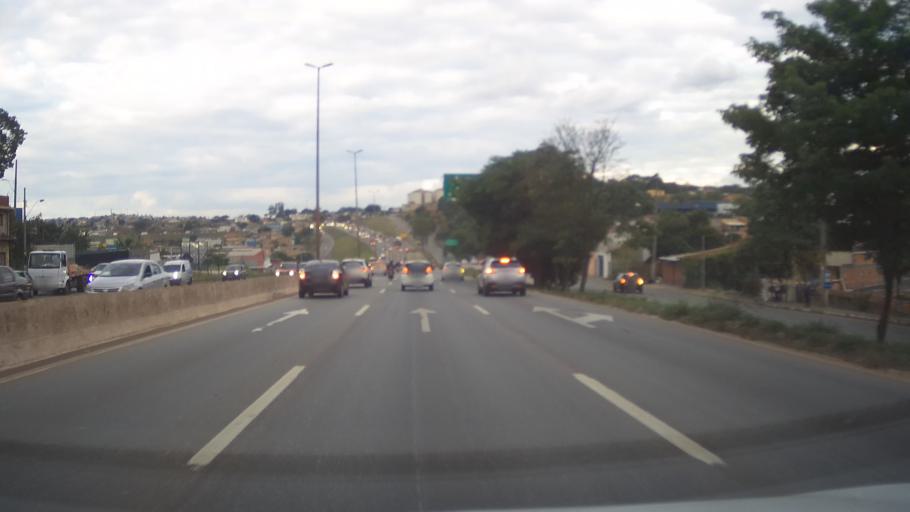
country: BR
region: Minas Gerais
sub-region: Contagem
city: Contagem
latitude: -19.9206
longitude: -44.0004
